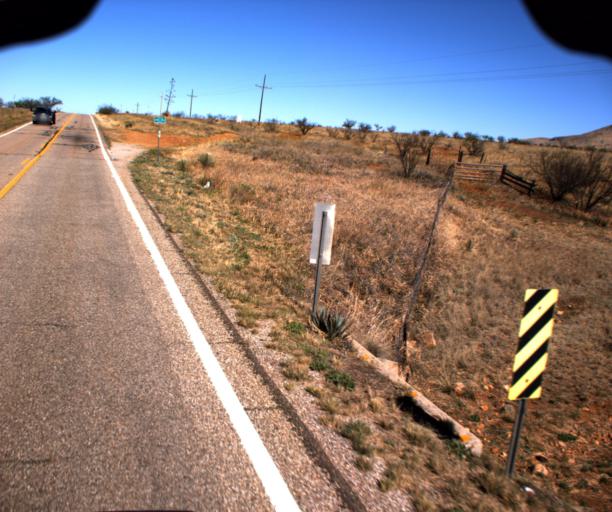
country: US
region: Arizona
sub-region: Cochise County
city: Huachuca City
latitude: 31.7110
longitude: -110.4519
